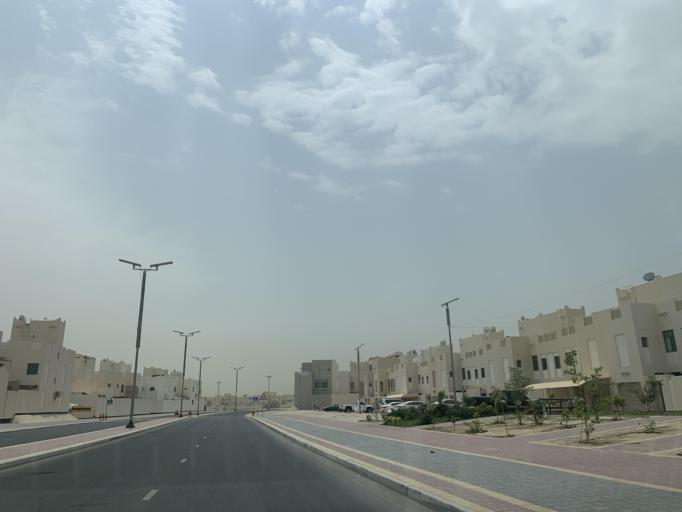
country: BH
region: Northern
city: Madinat `Isa
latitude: 26.1756
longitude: 50.5170
